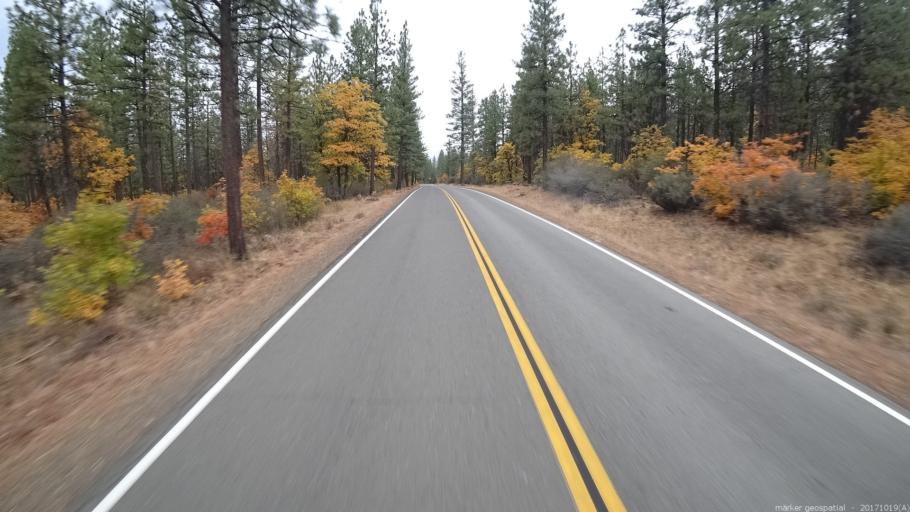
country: US
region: California
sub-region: Shasta County
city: Burney
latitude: 41.1769
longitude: -121.3621
